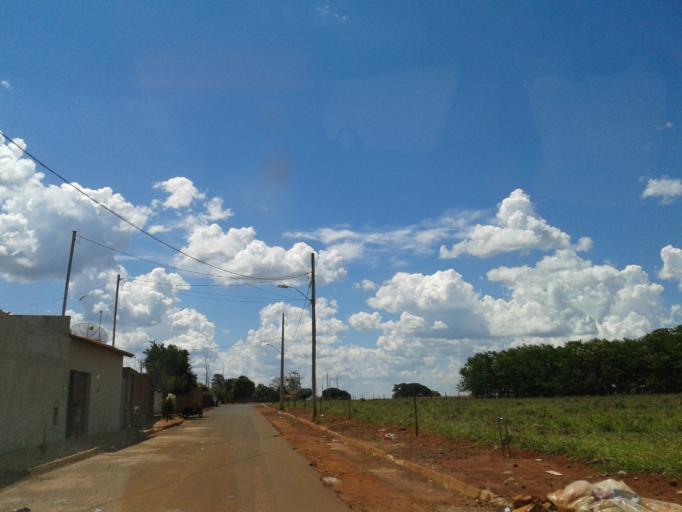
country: BR
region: Minas Gerais
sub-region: Centralina
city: Centralina
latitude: -18.7230
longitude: -49.1913
